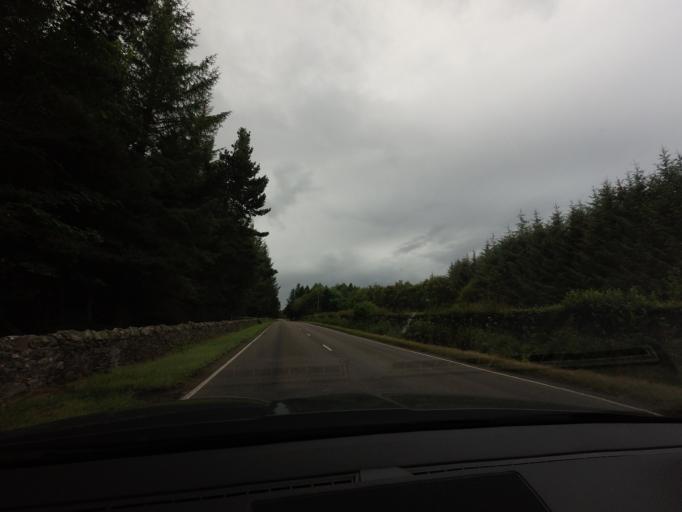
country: GB
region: Scotland
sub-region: Moray
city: Portknockie
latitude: 57.6866
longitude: -2.8760
